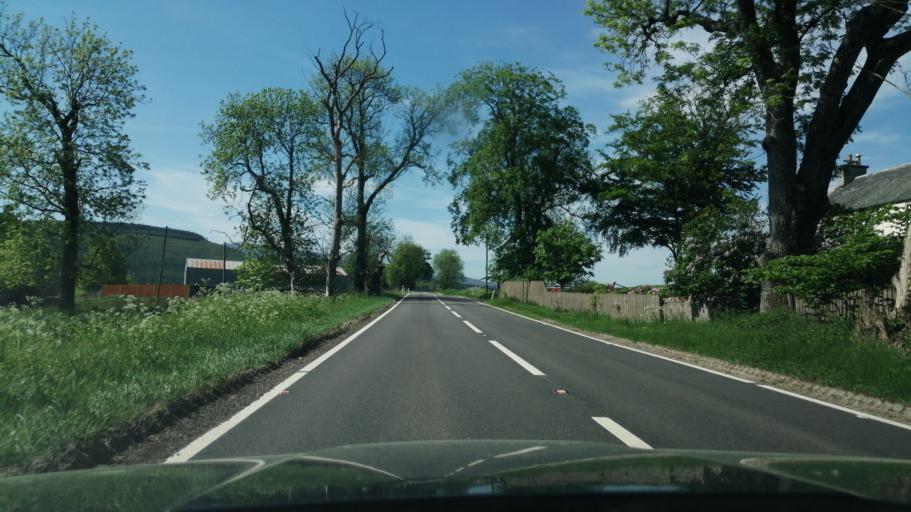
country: GB
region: Scotland
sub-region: Moray
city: Rothes
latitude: 57.4909
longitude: -3.1595
